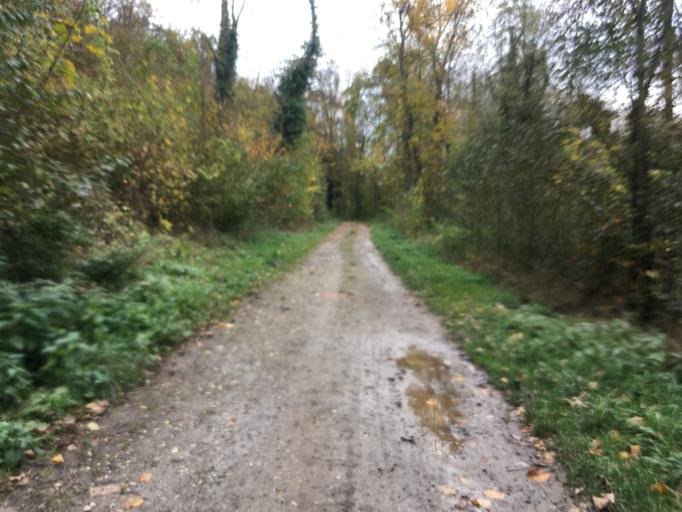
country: DE
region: Baden-Wuerttemberg
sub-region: Freiburg Region
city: Sasbach
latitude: 48.1062
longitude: 7.5890
